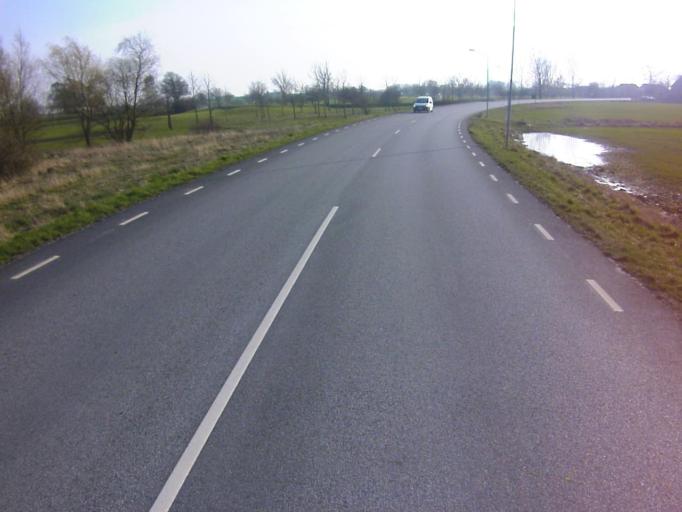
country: SE
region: Skane
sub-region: Kavlinge Kommun
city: Kaevlinge
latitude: 55.7961
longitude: 13.1484
